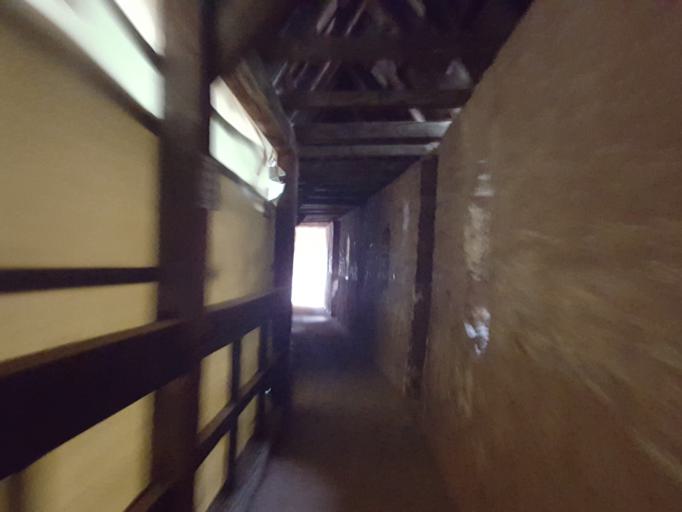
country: DE
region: Bavaria
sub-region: Swabia
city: Noerdlingen
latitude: 48.8522
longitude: 10.4837
